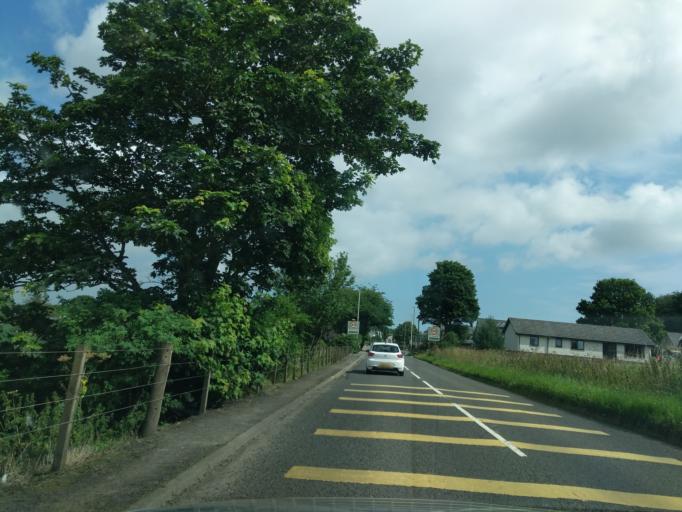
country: GB
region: Scotland
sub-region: Angus
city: Muirhead
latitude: 56.4981
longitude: -3.0739
